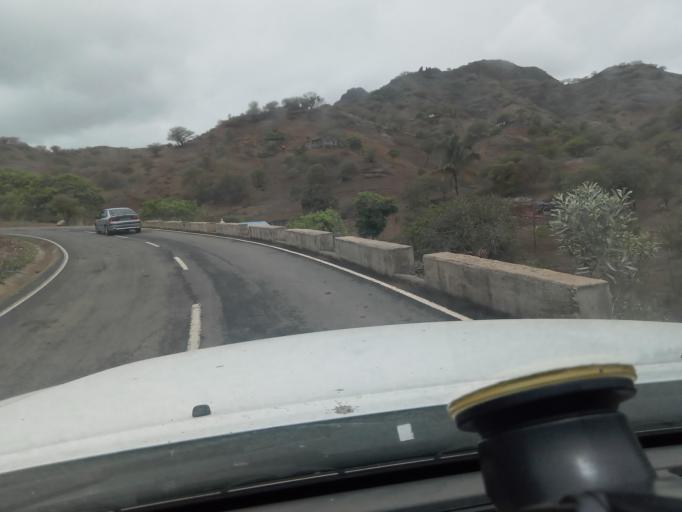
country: CV
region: Sao Miguel
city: Calheta
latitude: 15.1461
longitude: -23.6198
